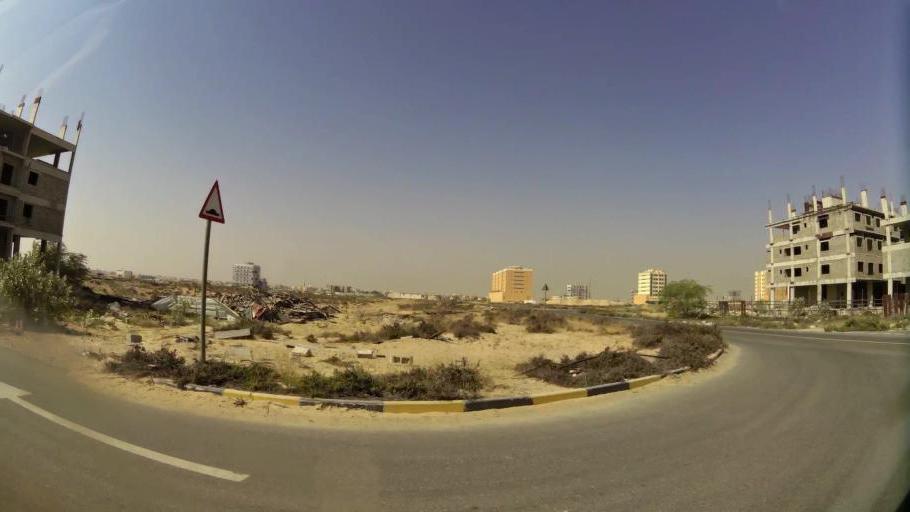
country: AE
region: Ajman
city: Ajman
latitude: 25.4269
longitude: 55.5387
